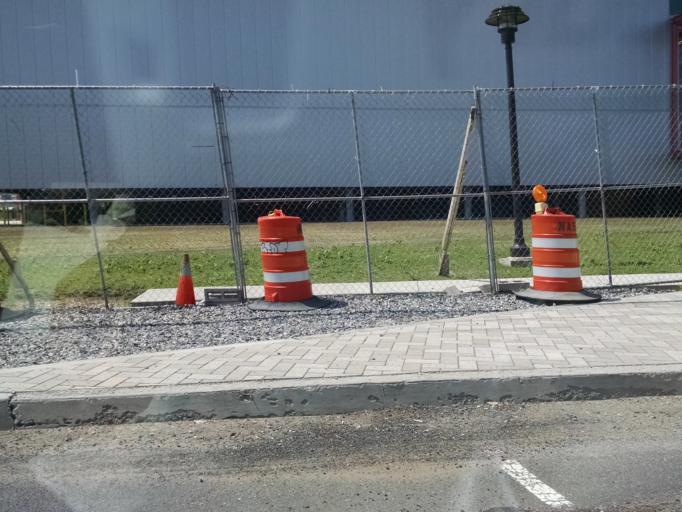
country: US
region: New York
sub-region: Richmond County
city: Staten Island
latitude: 40.5824
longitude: -74.0746
